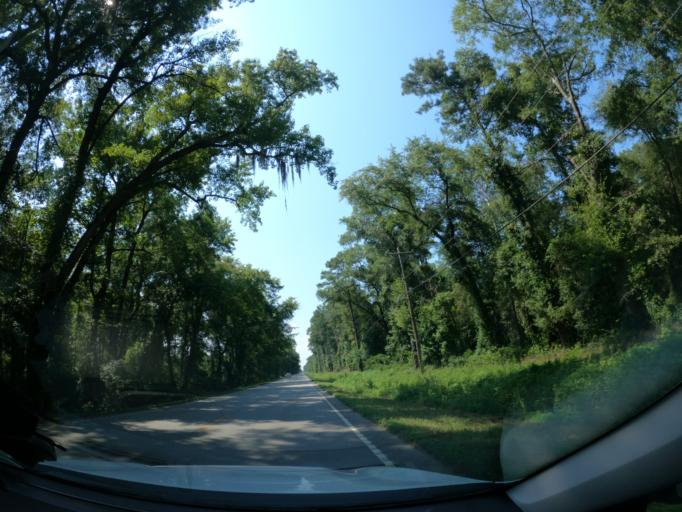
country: US
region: South Carolina
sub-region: Richland County
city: Hopkins
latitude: 33.9100
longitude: -80.9378
